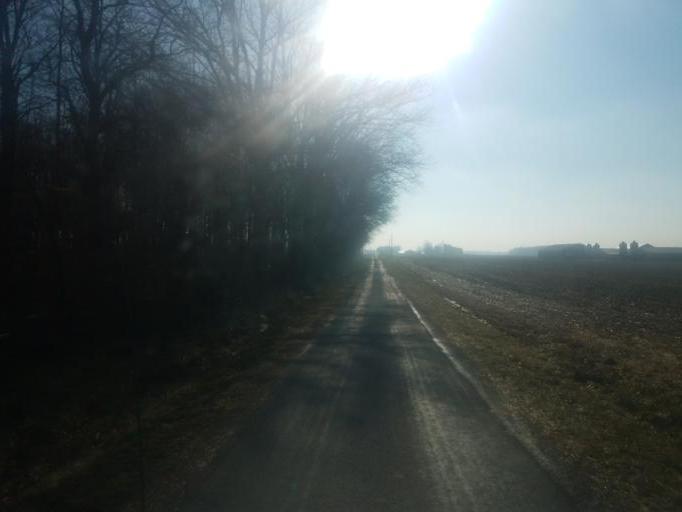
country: US
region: Ohio
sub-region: Crawford County
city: Bucyrus
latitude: 40.9575
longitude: -83.0743
